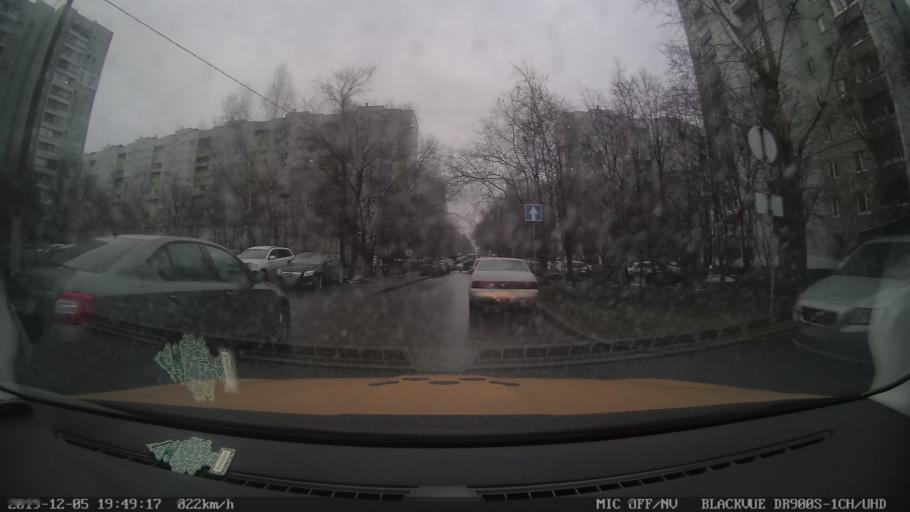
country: RU
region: Moscow
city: Lianozovo
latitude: 55.9053
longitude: 37.5802
